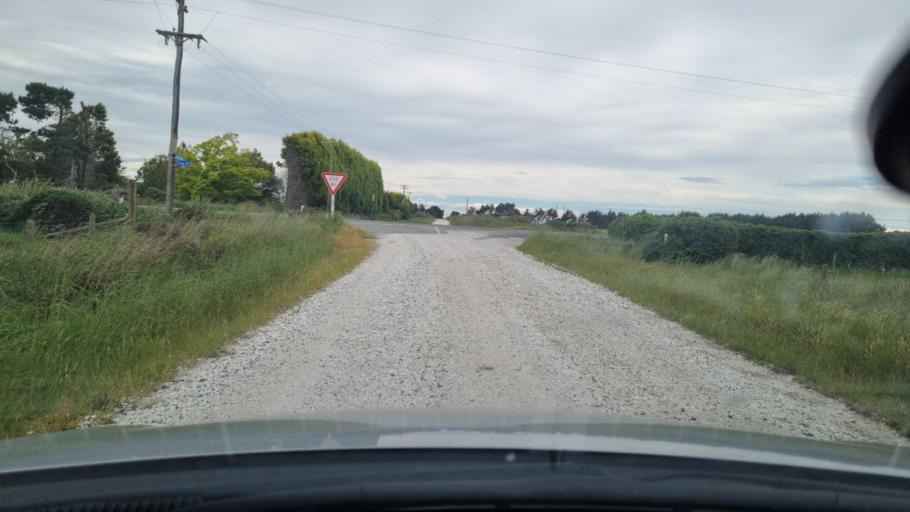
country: NZ
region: Southland
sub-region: Invercargill City
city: Invercargill
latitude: -46.4964
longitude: 168.4187
